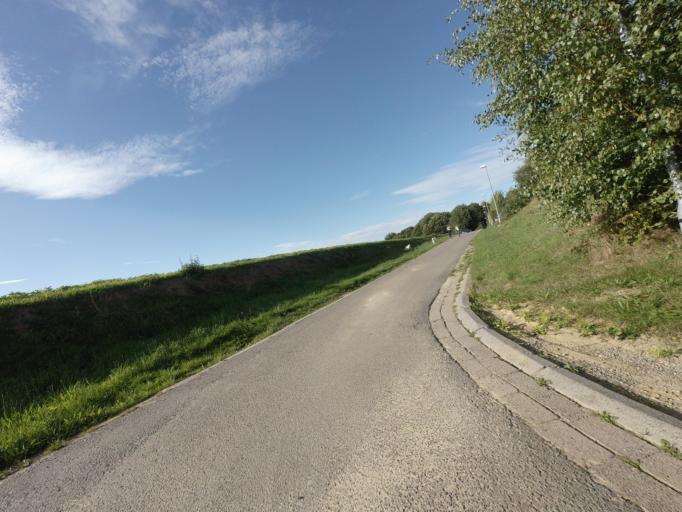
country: BE
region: Flanders
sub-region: Provincie Vlaams-Brabant
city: Herent
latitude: 50.8912
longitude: 4.6595
